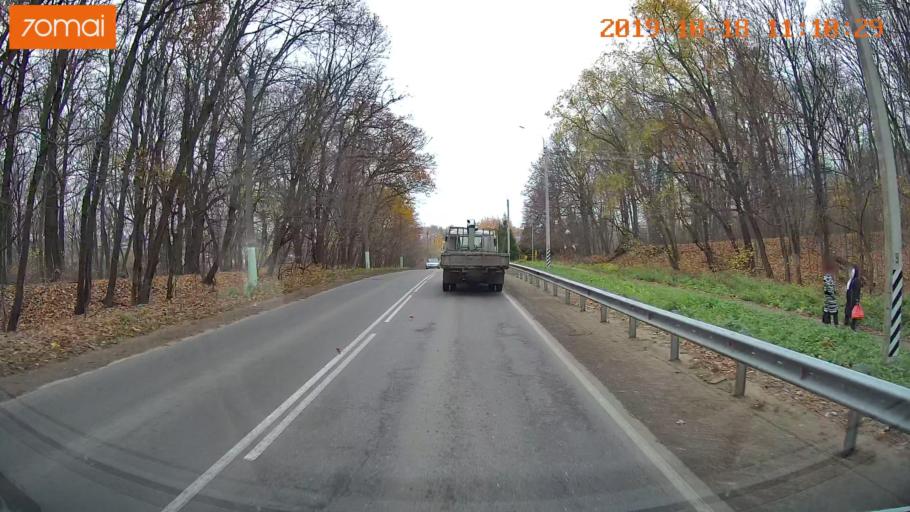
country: RU
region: Tula
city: Kimovsk
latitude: 53.9558
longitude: 38.5388
